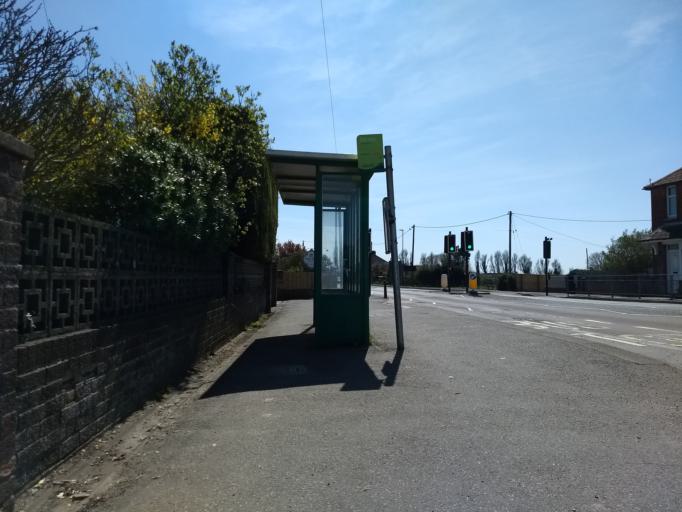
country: GB
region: England
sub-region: Isle of Wight
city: Northwood
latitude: 50.7386
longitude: -1.3077
